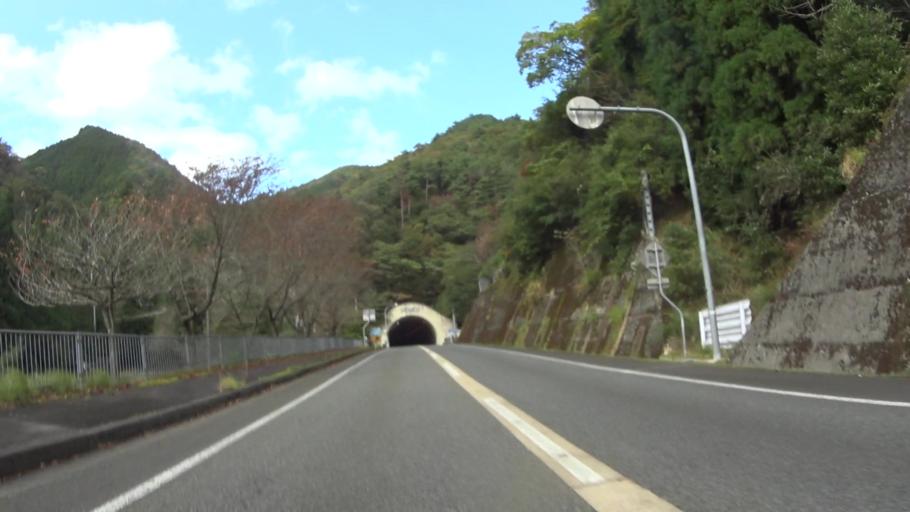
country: JP
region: Hyogo
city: Toyooka
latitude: 35.5231
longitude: 134.9875
